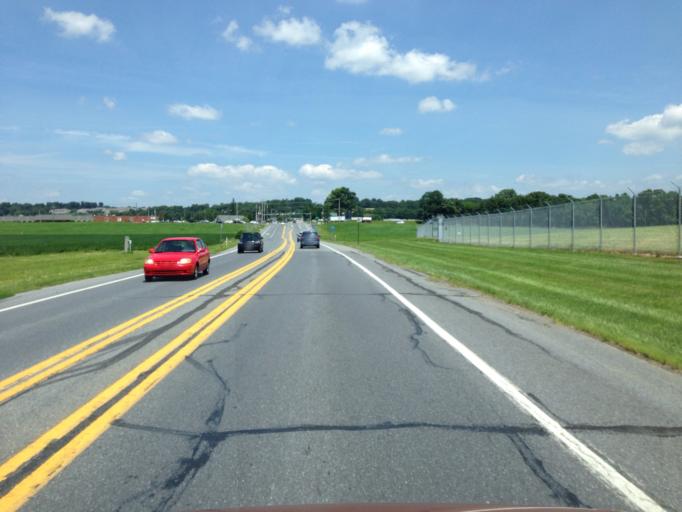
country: US
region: Pennsylvania
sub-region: Lancaster County
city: Lititz
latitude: 40.1232
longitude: -76.3053
